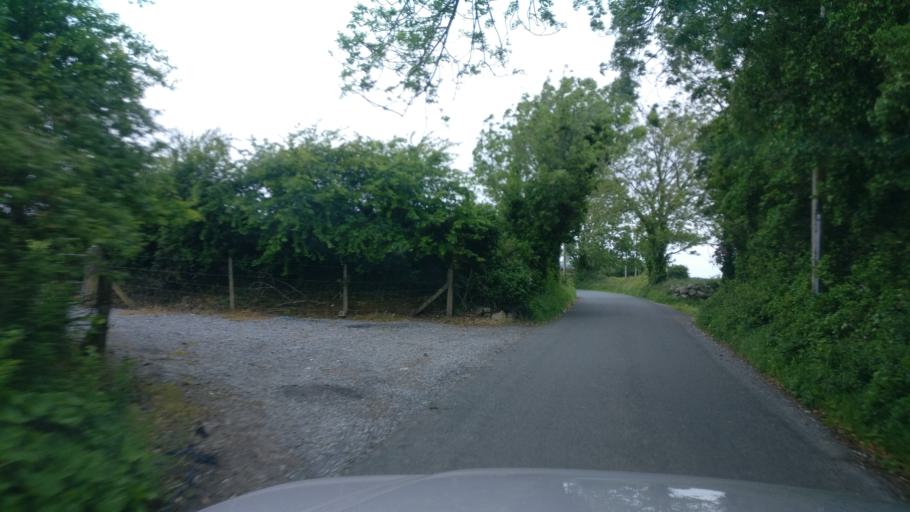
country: IE
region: Connaught
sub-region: County Galway
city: Loughrea
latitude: 53.1216
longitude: -8.4387
